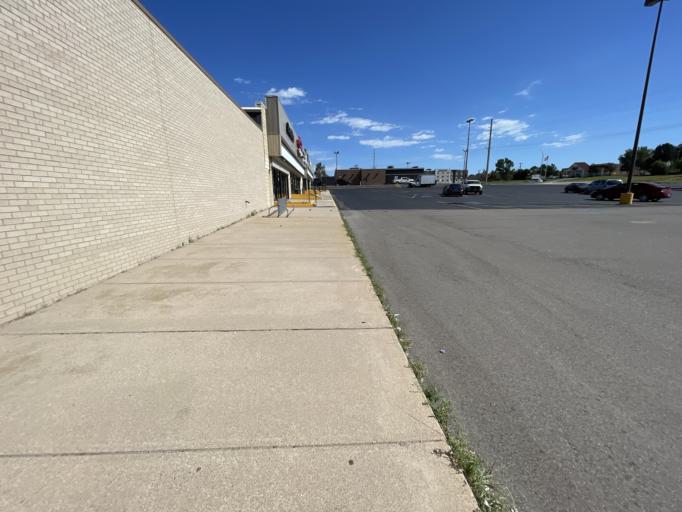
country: US
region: Nebraska
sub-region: Red Willow County
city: McCook
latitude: 40.2019
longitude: -100.6461
